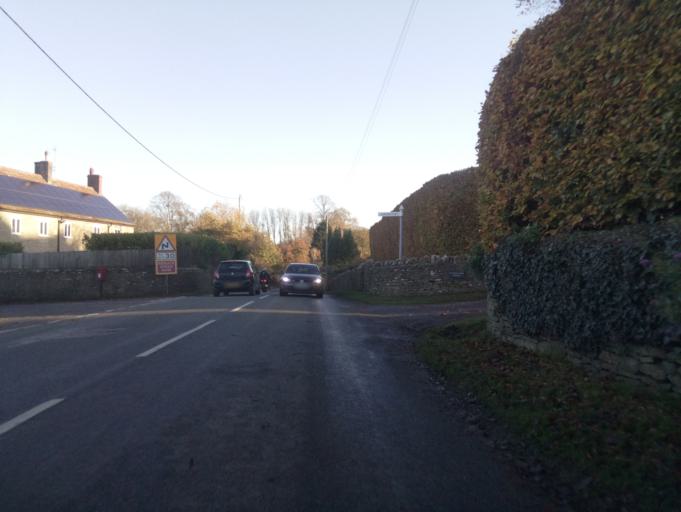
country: GB
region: England
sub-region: Somerset
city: Wincanton
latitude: 51.0127
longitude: -2.4309
